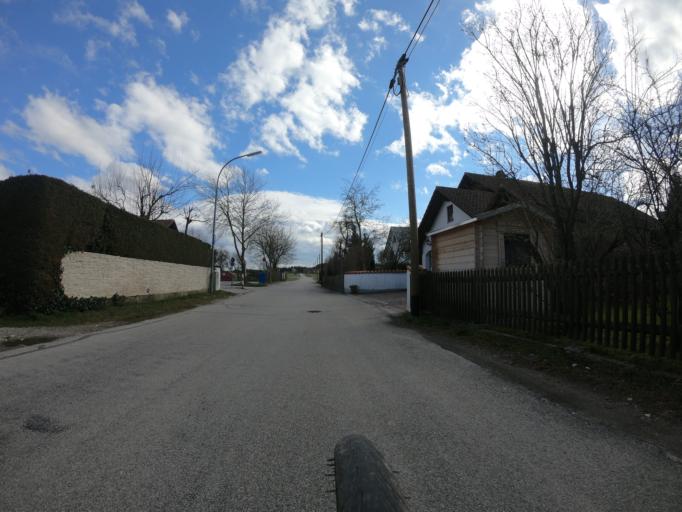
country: DE
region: Bavaria
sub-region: Upper Bavaria
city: Landsberied
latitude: 48.1779
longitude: 11.1927
